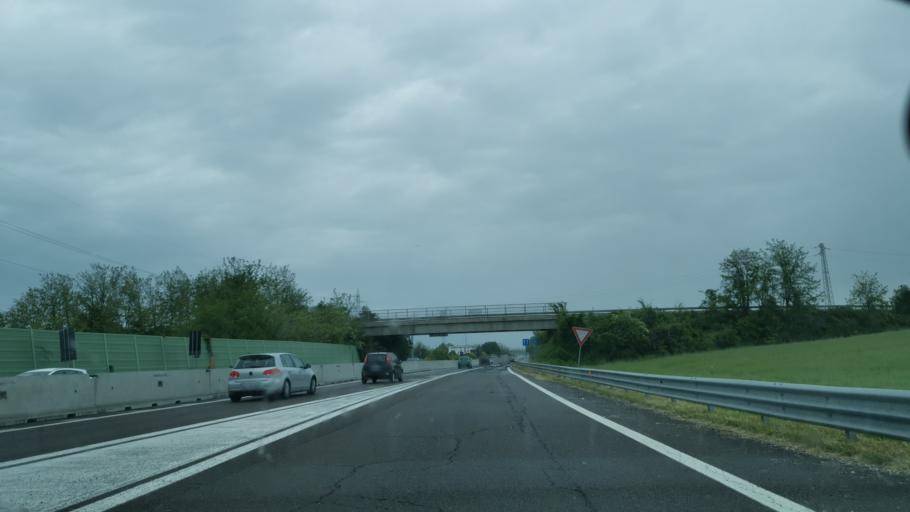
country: IT
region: Veneto
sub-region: Provincia di Verona
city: Castelnuovo del Garda
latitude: 45.4406
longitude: 10.7442
